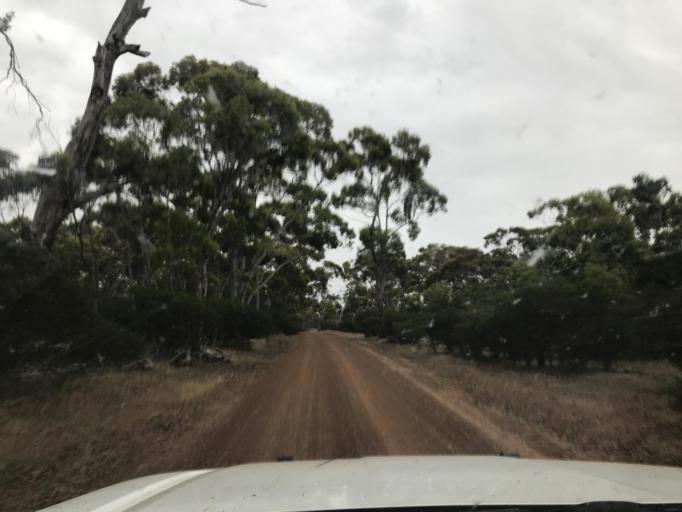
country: AU
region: South Australia
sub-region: Wattle Range
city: Penola
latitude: -37.0938
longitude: 141.5097
